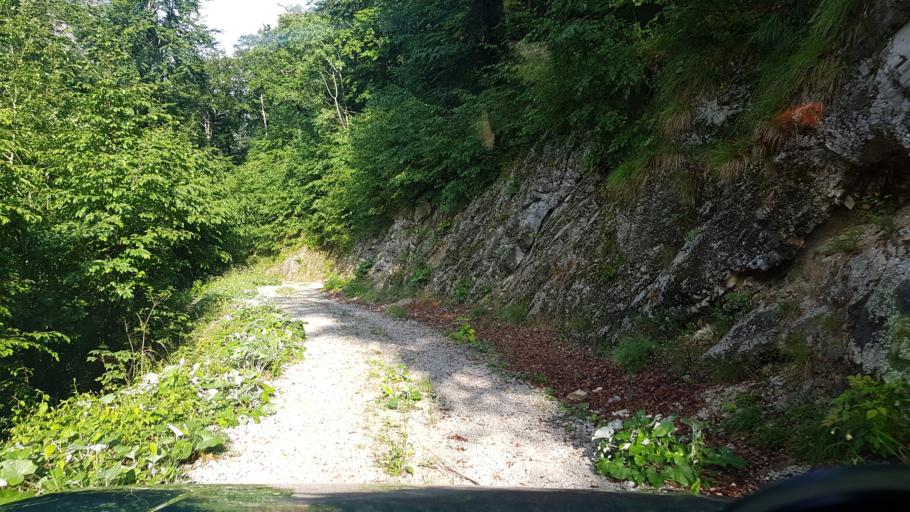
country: IT
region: Friuli Venezia Giulia
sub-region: Provincia di Udine
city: Lusevera
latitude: 46.3026
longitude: 13.3102
